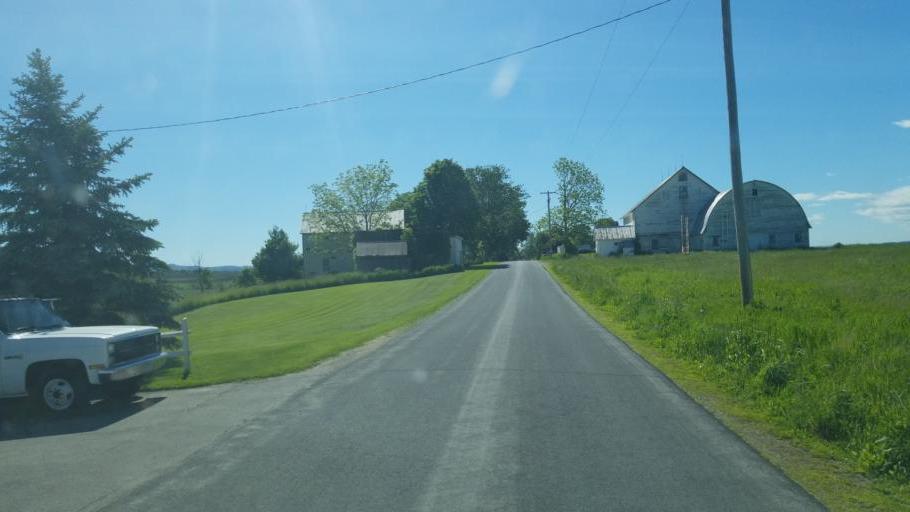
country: US
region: New York
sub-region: Montgomery County
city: Fort Plain
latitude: 42.9150
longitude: -74.6264
